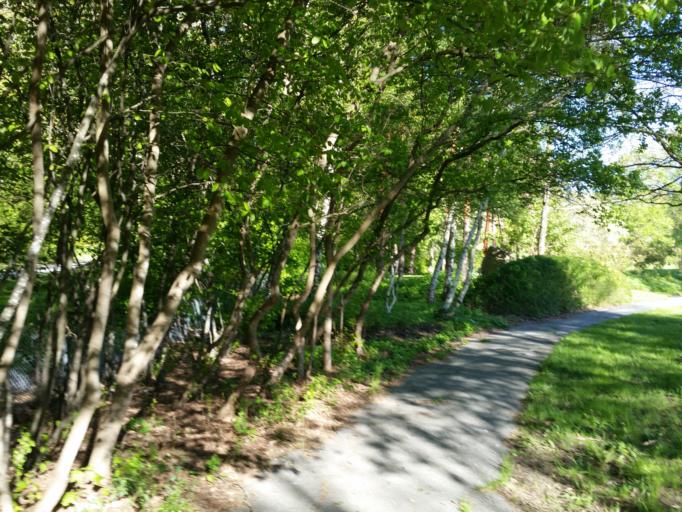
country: SE
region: Stockholm
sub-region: Sundbybergs Kommun
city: Sundbyberg
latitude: 59.3747
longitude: 17.9596
